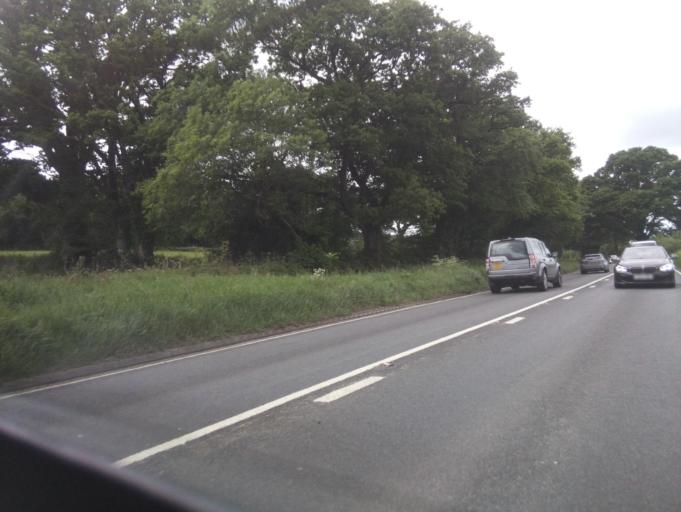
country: GB
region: England
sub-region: Devon
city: Axminster
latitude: 50.7834
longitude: -3.0450
